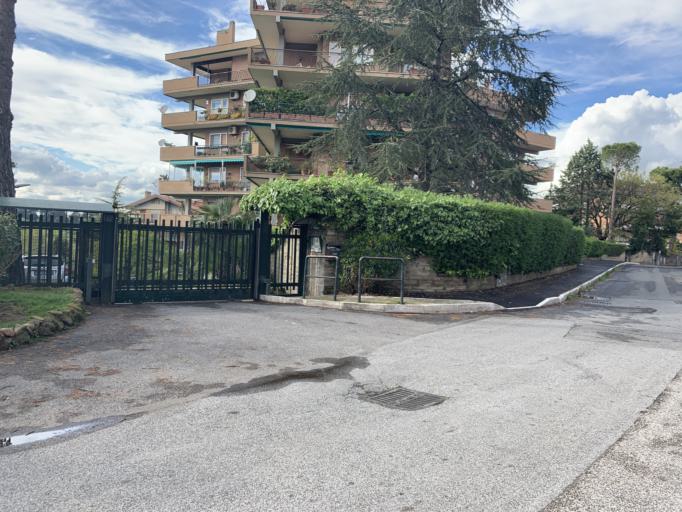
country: VA
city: Vatican City
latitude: 41.8801
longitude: 12.4144
